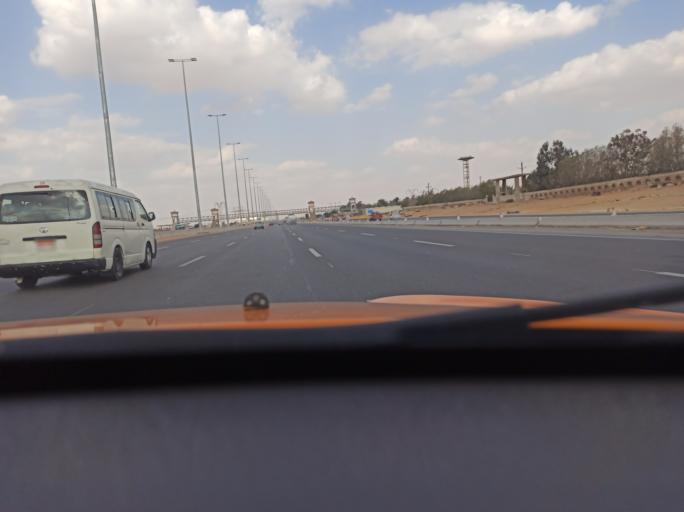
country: EG
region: Eastern Province
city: Bilbays
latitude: 30.1849
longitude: 31.6222
